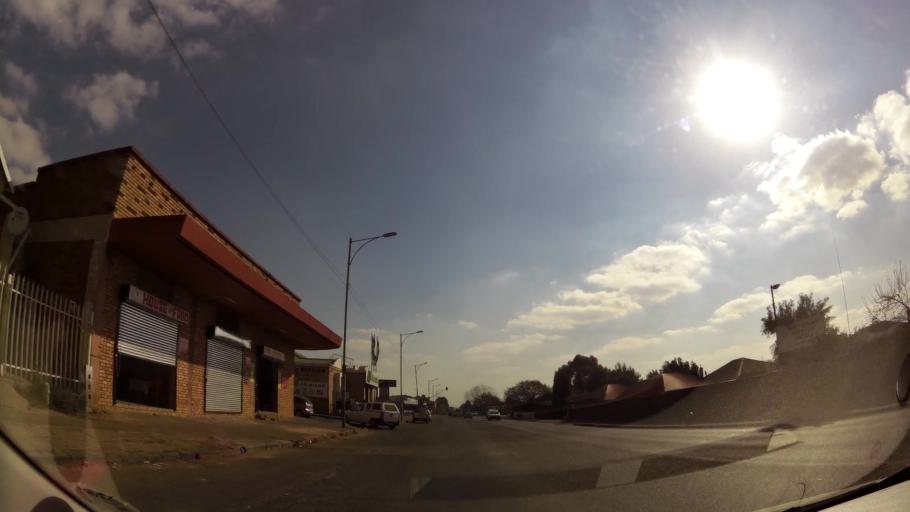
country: ZA
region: Gauteng
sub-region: West Rand District Municipality
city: Krugersdorp
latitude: -26.1068
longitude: 27.7765
